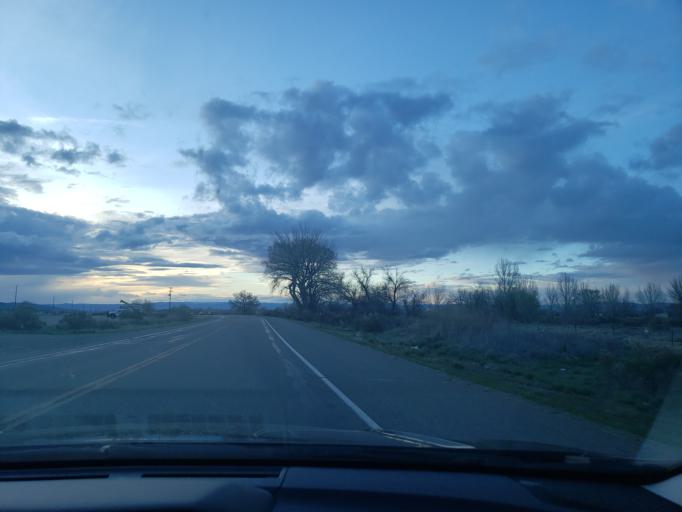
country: US
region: Colorado
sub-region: Mesa County
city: Fruita
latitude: 39.1430
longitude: -108.7086
